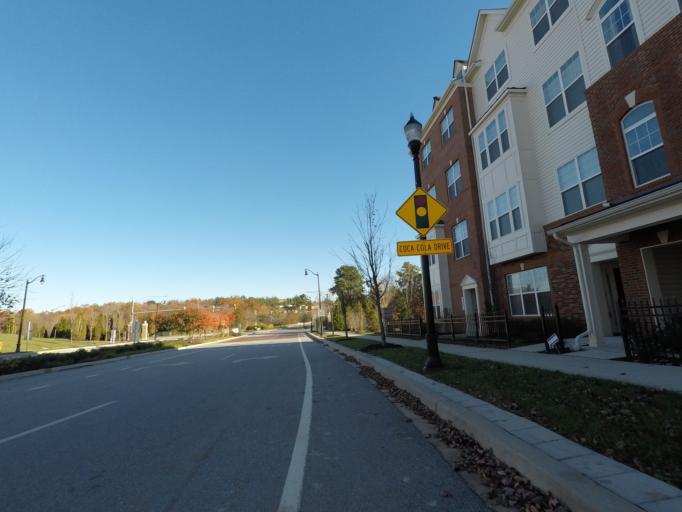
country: US
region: Maryland
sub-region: Howard County
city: Hanover
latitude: 39.1822
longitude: -76.7363
